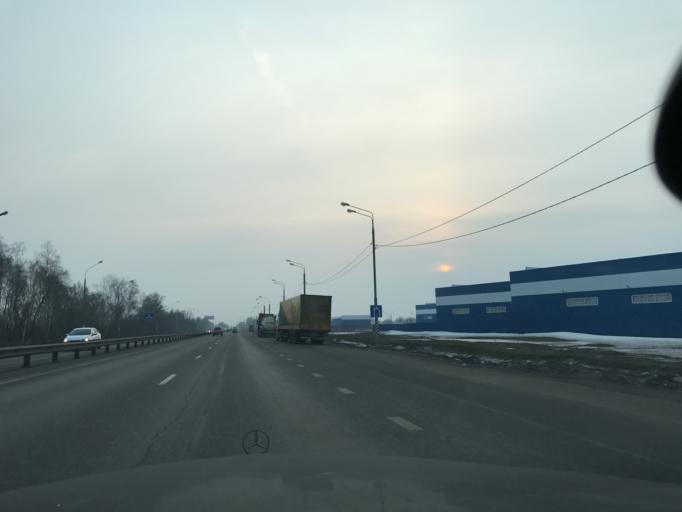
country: RU
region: Moskovskaya
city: Obukhovo
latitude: 55.8271
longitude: 38.2429
